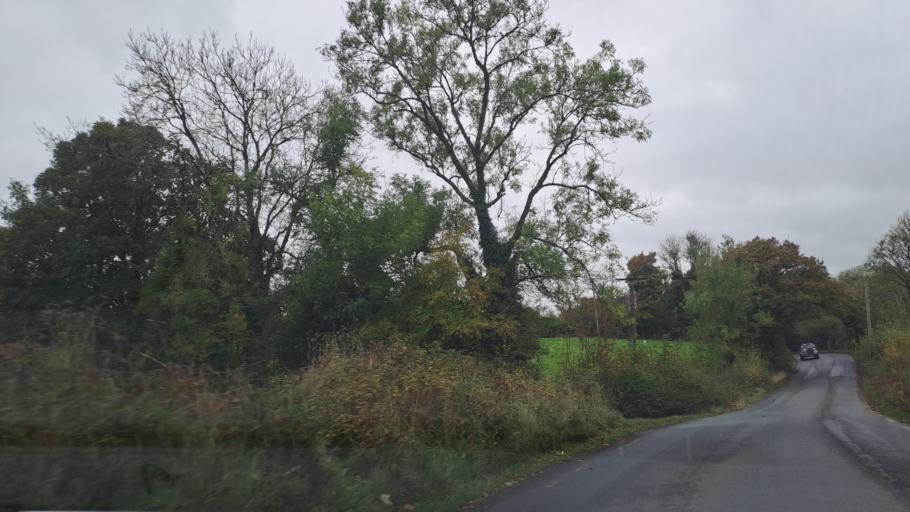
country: IE
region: Ulster
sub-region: An Cabhan
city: Cootehill
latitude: 54.0171
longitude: -7.0513
